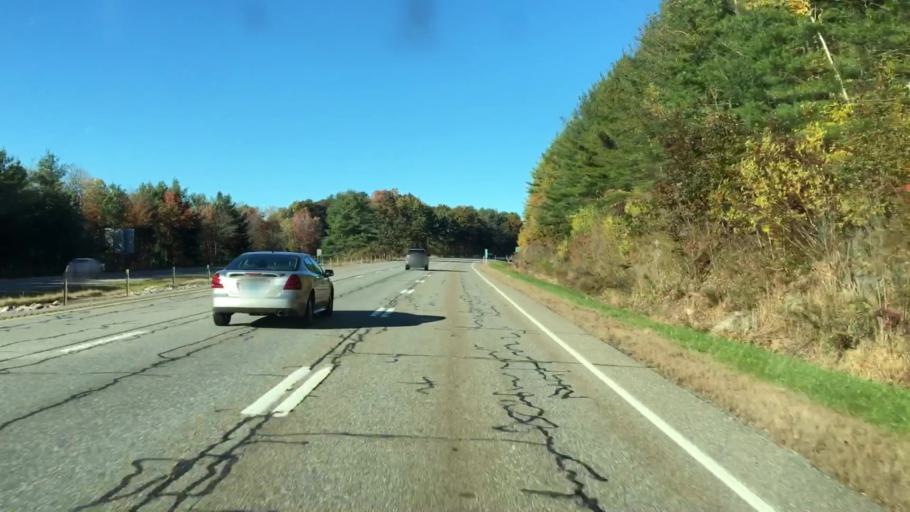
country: US
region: Connecticut
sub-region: Litchfield County
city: Torrington
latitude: 41.7700
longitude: -73.1148
